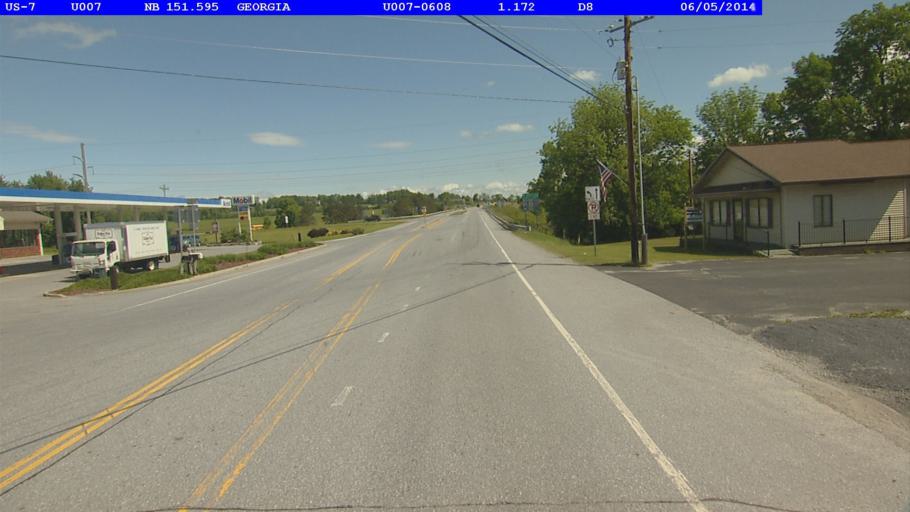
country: US
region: Vermont
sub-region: Chittenden County
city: Milton
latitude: 44.6958
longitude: -73.1074
